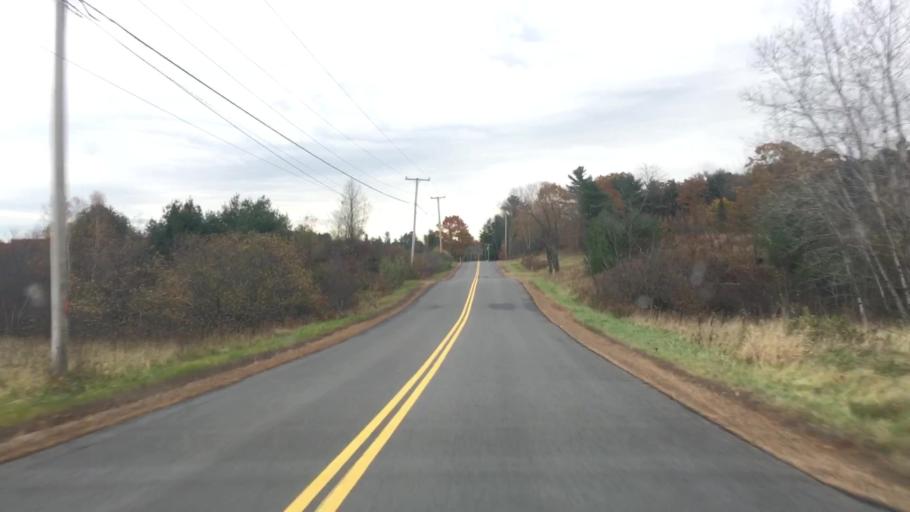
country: US
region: Maine
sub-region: Kennebec County
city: Pittston
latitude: 44.1694
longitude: -69.7176
